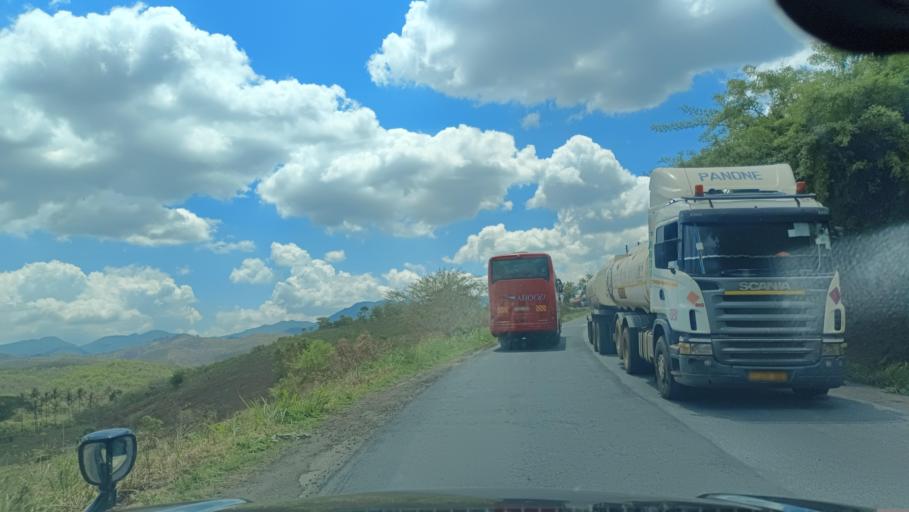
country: TZ
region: Morogoro
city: Mikumi
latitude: -7.4547
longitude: 36.9213
